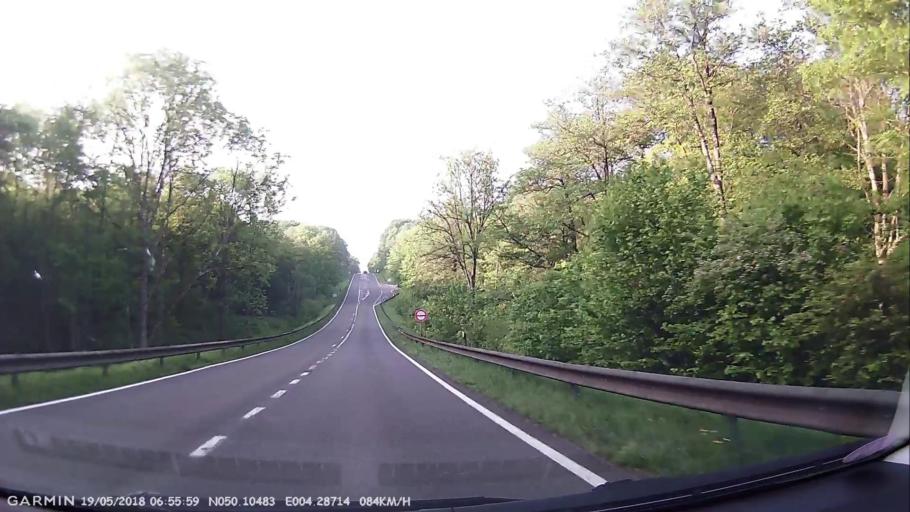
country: BE
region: Wallonia
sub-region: Province du Hainaut
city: Froidchapelle
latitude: 50.1047
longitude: 4.2872
